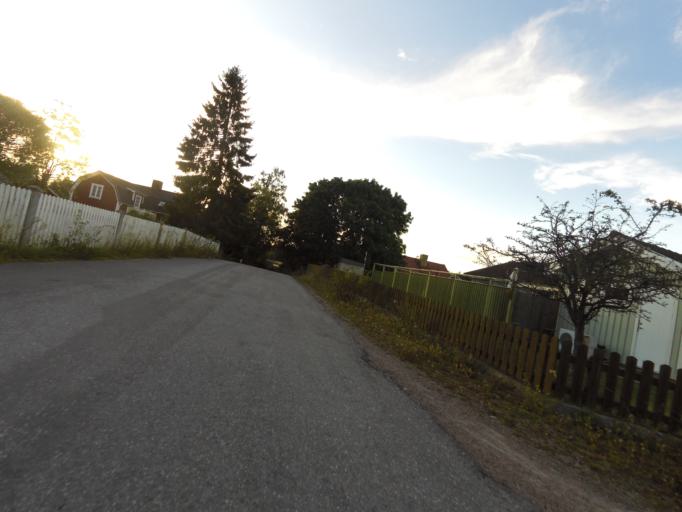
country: SE
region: Gaevleborg
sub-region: Gavle Kommun
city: Gavle
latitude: 60.7304
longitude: 17.1765
